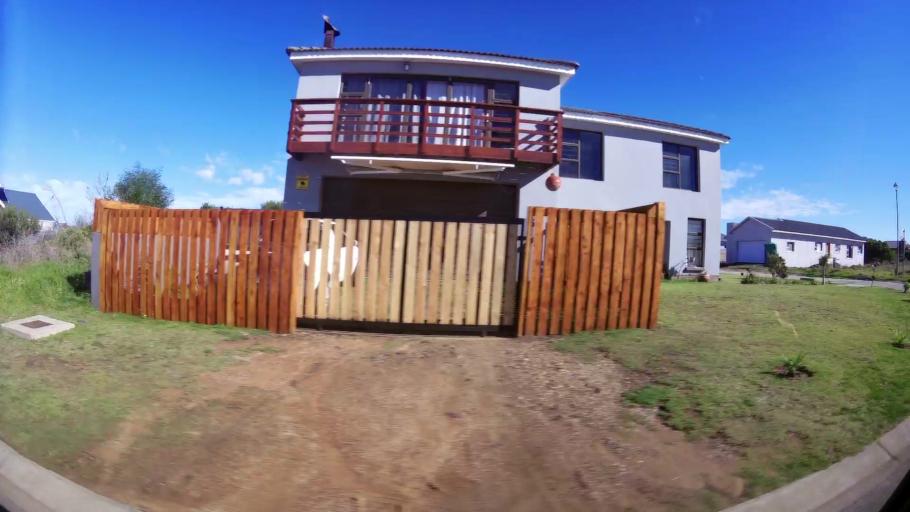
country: ZA
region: Eastern Cape
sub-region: Cacadu District Municipality
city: Jeffrey's Bay
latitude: -34.0364
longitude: 24.9082
